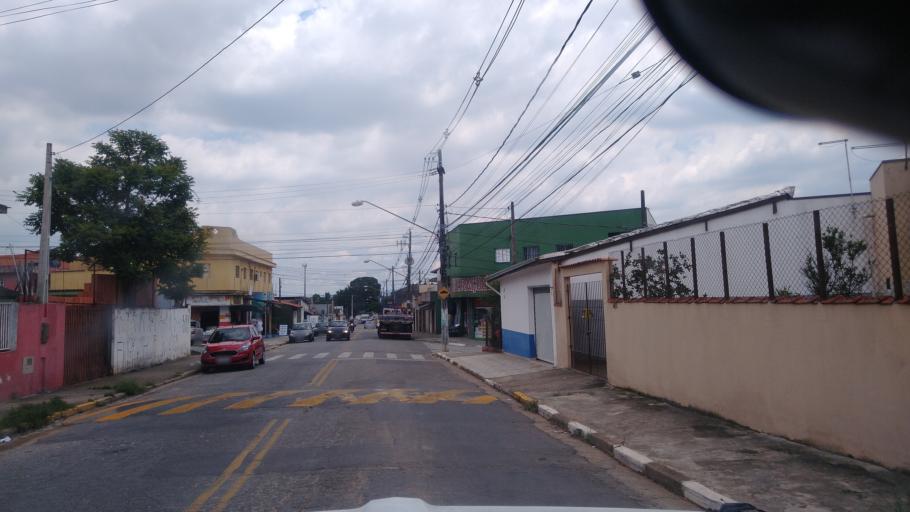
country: BR
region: Sao Paulo
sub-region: Suzano
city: Suzano
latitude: -23.5570
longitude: -46.3221
